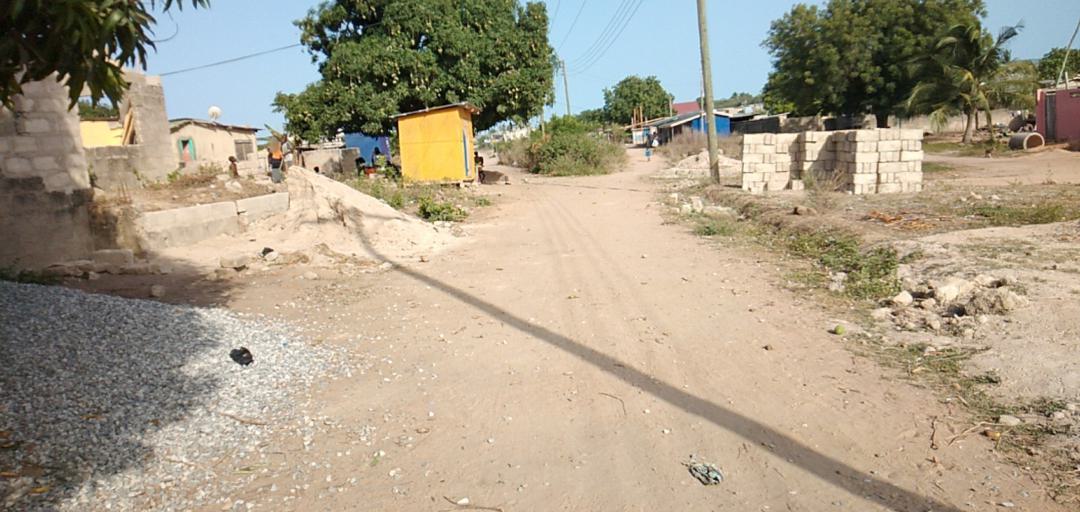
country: GH
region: Central
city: Winneba
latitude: 5.3584
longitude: -0.6214
